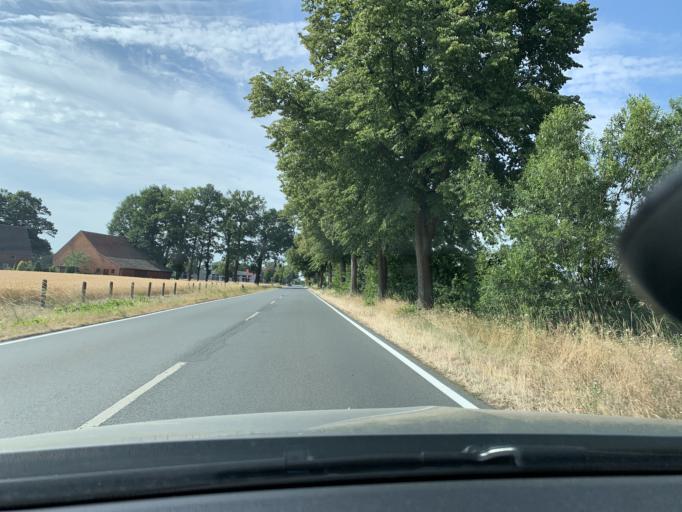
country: DE
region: North Rhine-Westphalia
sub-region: Regierungsbezirk Detmold
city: Langenberg
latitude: 51.7463
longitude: 8.3811
